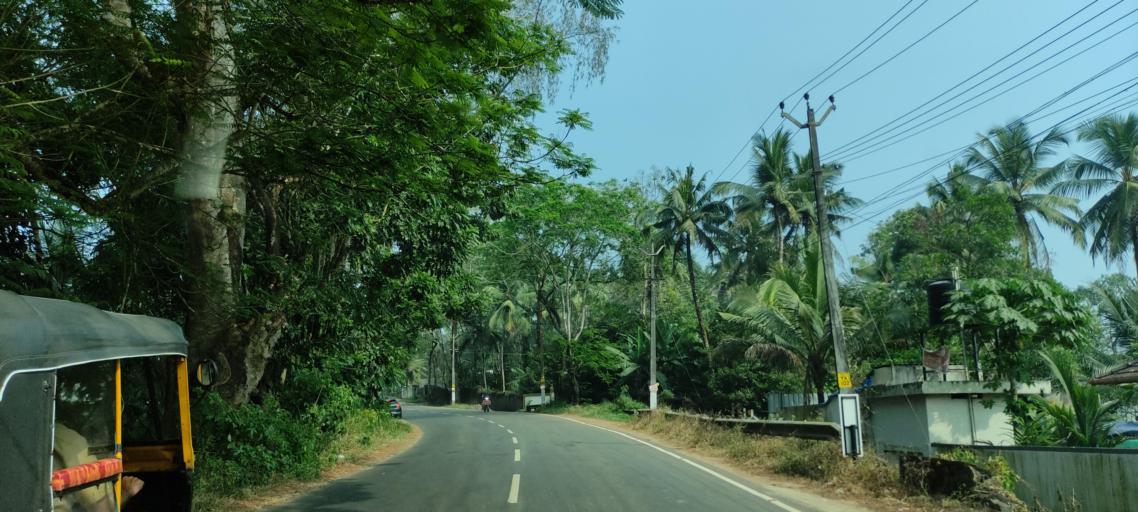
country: IN
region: Kerala
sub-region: Ernakulam
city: Piravam
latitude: 9.7948
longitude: 76.4684
